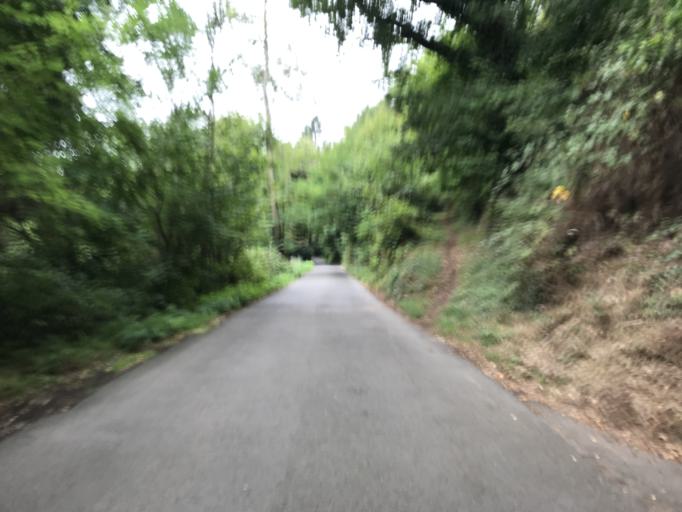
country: DE
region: Rheinland-Pfalz
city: Bad Kreuznach
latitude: 49.8330
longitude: 7.8481
